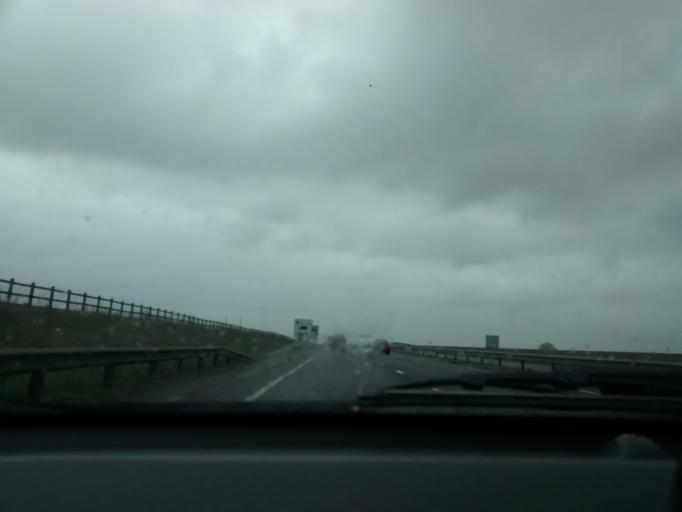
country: GB
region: England
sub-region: Suffolk
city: Stowmarket
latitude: 52.2107
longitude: 0.9657
